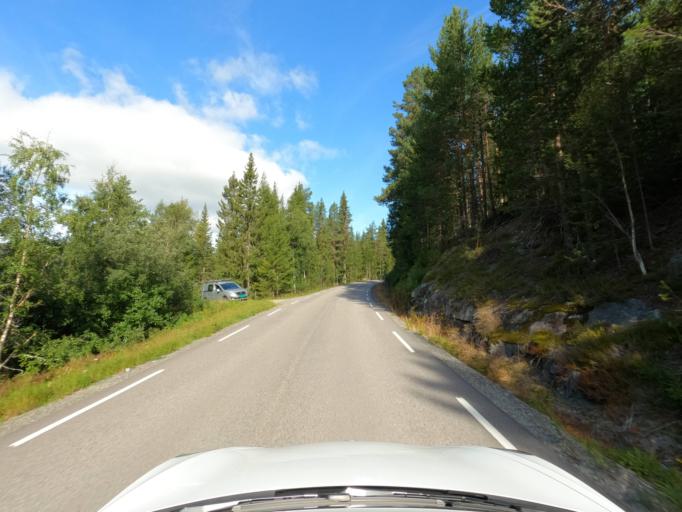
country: NO
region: Telemark
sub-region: Tinn
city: Rjukan
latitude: 60.1093
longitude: 8.7285
